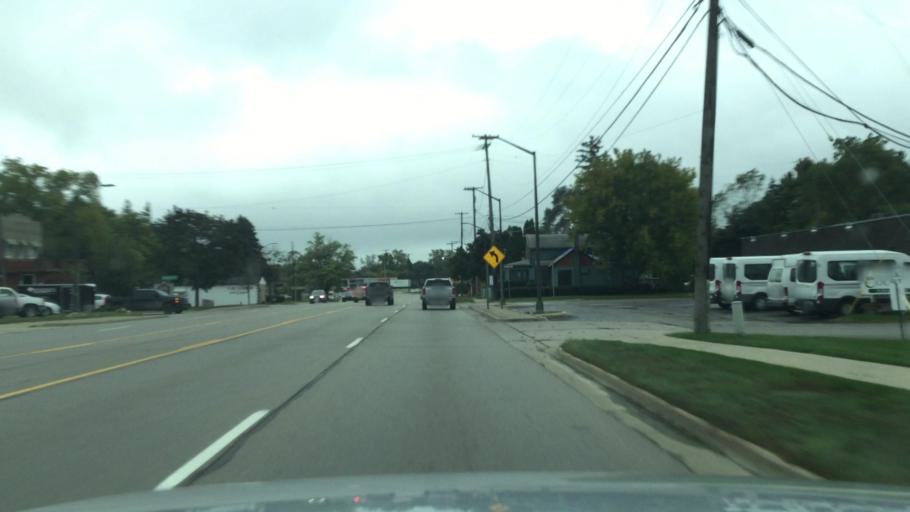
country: US
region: Michigan
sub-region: Oakland County
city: Waterford
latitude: 42.7052
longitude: -83.4047
